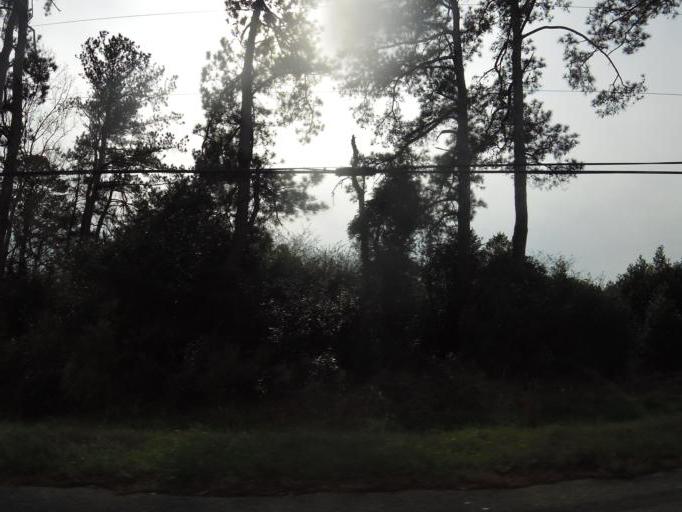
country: US
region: Alabama
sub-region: Houston County
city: Cowarts
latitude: 31.1962
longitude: -85.3327
